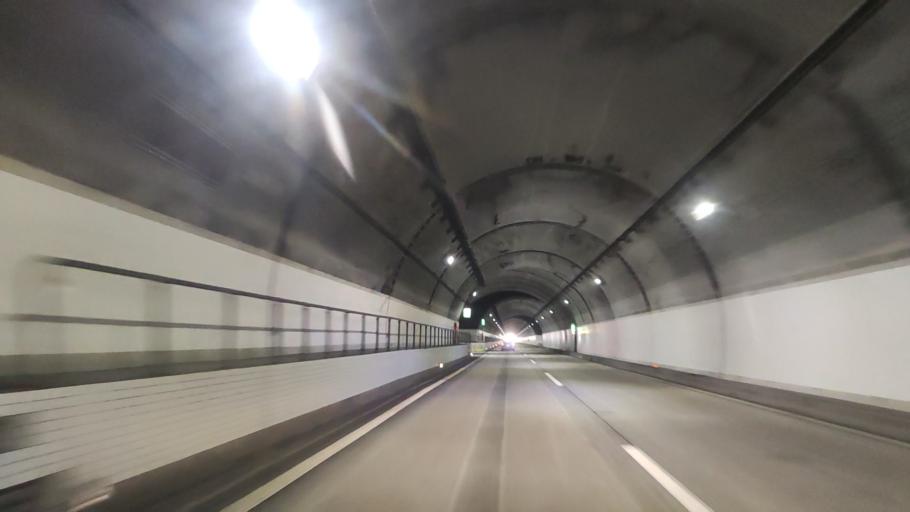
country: JP
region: Ehime
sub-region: Shikoku-chuo Shi
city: Matsuyama
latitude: 33.8231
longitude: 132.9695
